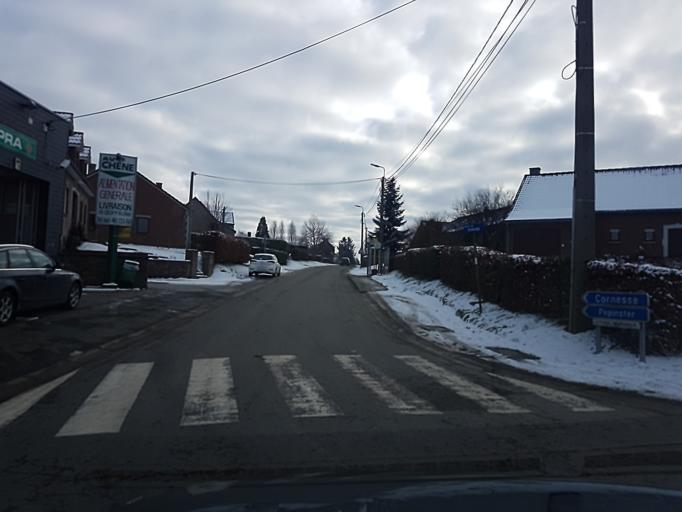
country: BE
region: Wallonia
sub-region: Province de Liege
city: Pepinster
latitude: 50.5842
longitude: 5.7878
